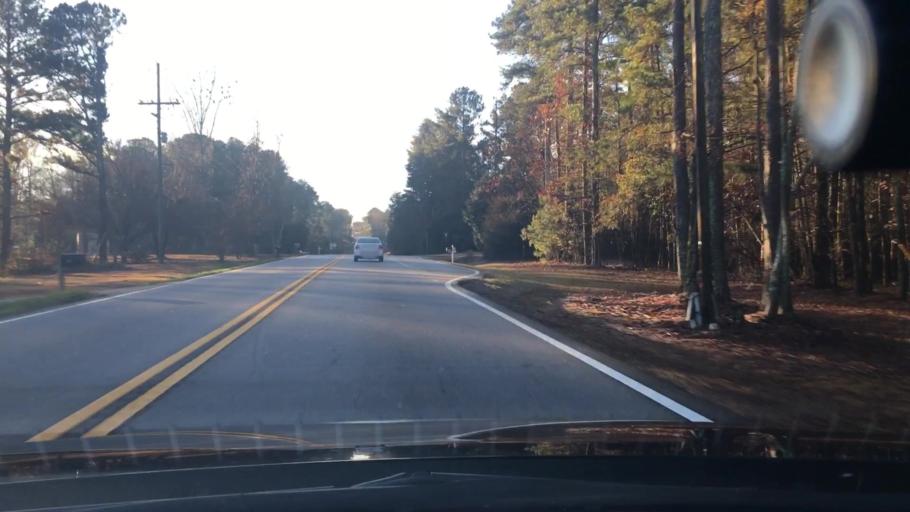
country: US
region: Georgia
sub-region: Fayette County
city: Peachtree City
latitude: 33.4008
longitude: -84.6812
